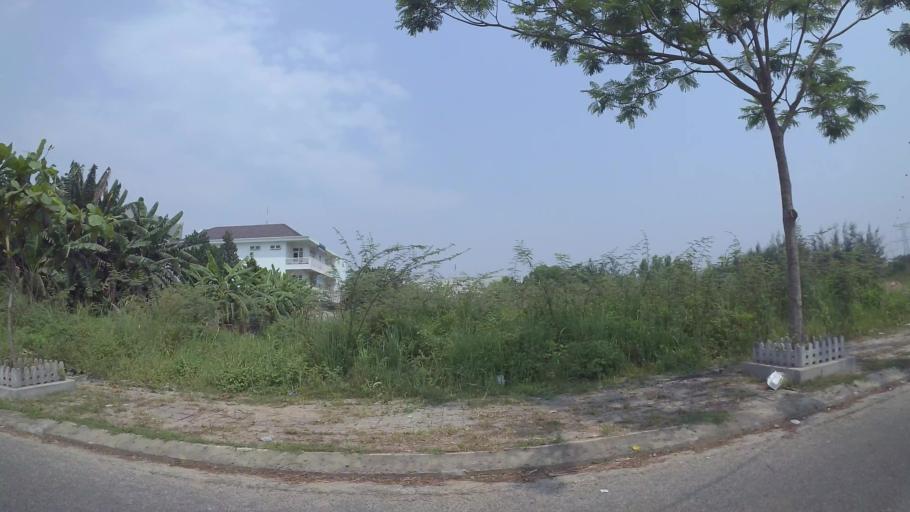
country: VN
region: Da Nang
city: Cam Le
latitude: 16.0022
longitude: 108.2113
